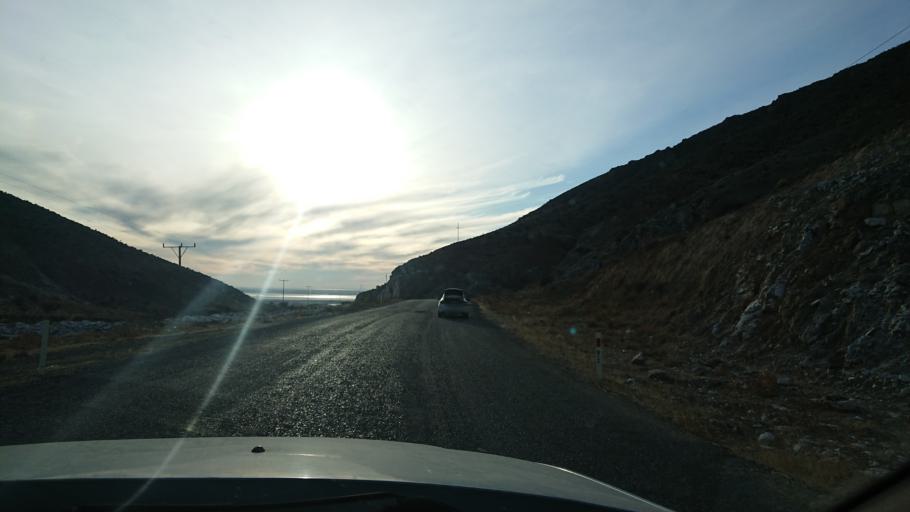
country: TR
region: Ankara
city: Sereflikochisar
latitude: 38.7496
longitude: 33.6887
